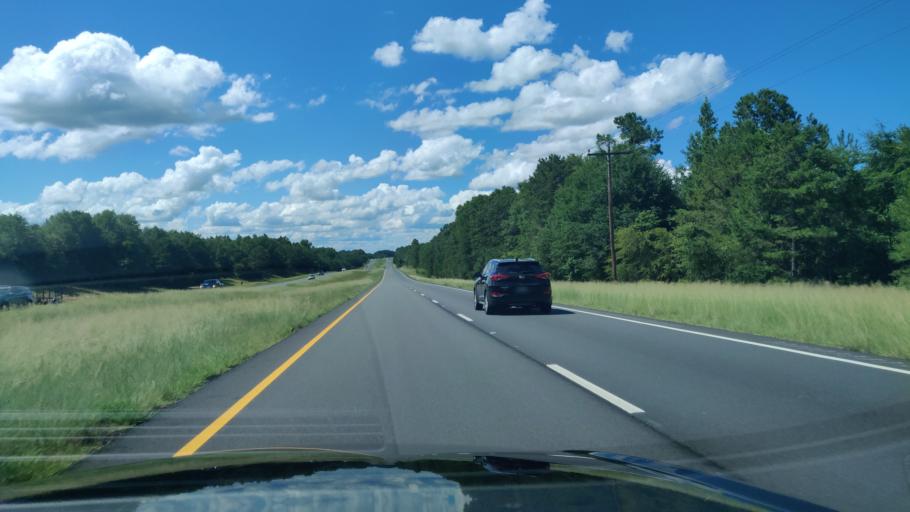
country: US
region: Georgia
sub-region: Stewart County
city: Richland
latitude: 32.2025
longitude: -84.7026
